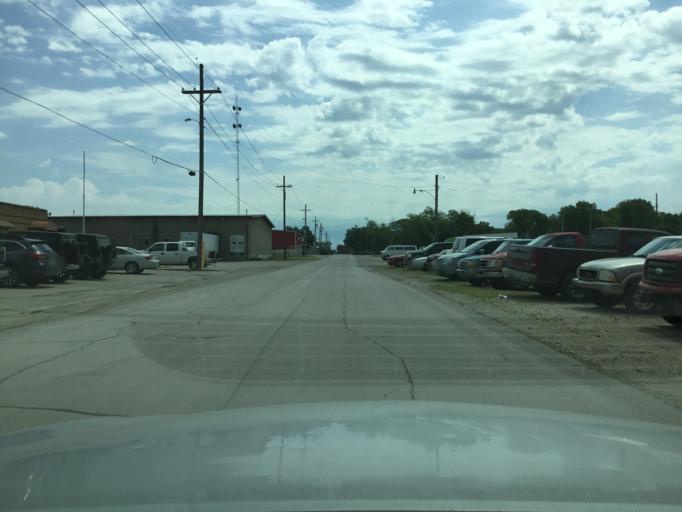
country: US
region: Kansas
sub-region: Montgomery County
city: Coffeyville
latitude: 37.0288
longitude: -95.6299
